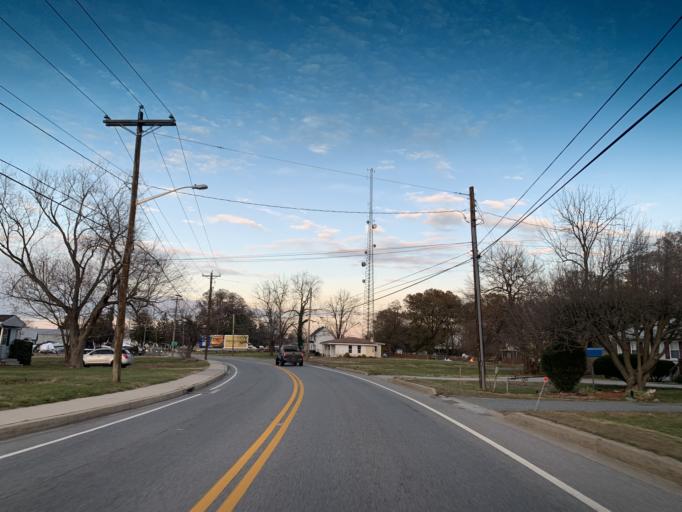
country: US
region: Delaware
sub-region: New Castle County
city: Middletown
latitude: 39.4010
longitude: -75.8690
